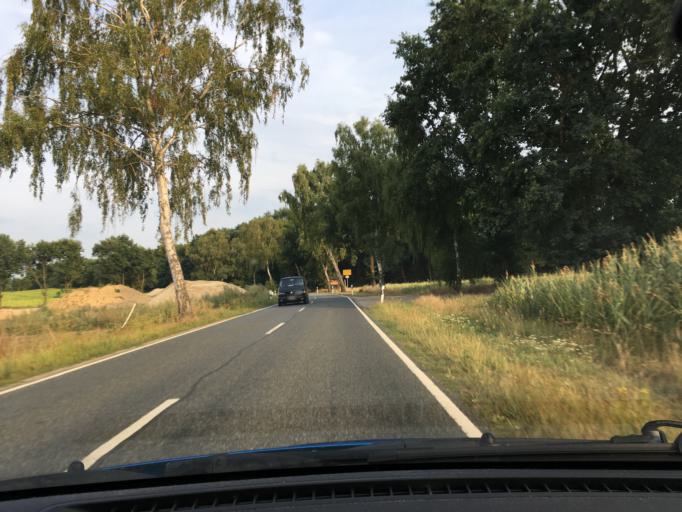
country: DE
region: Lower Saxony
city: Toppenstedt
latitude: 53.3028
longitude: 10.0898
